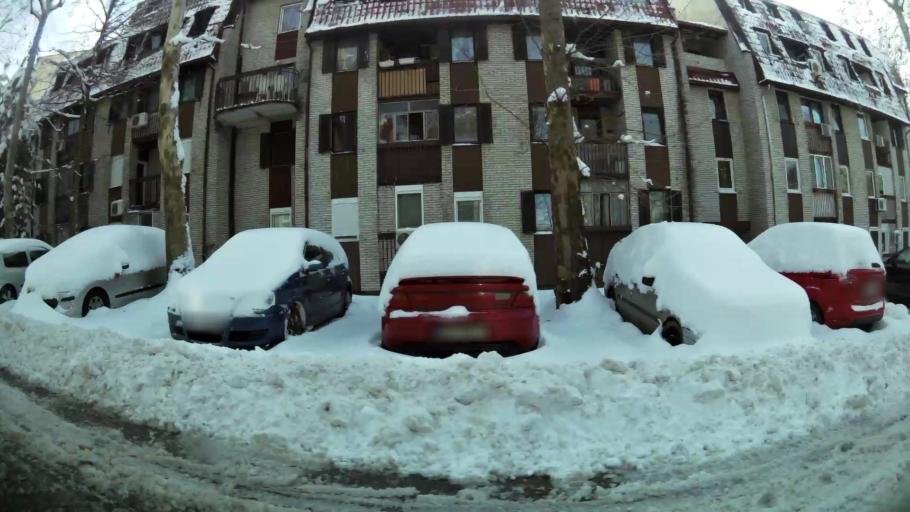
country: RS
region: Central Serbia
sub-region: Belgrade
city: Zvezdara
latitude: 44.7875
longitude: 20.5397
